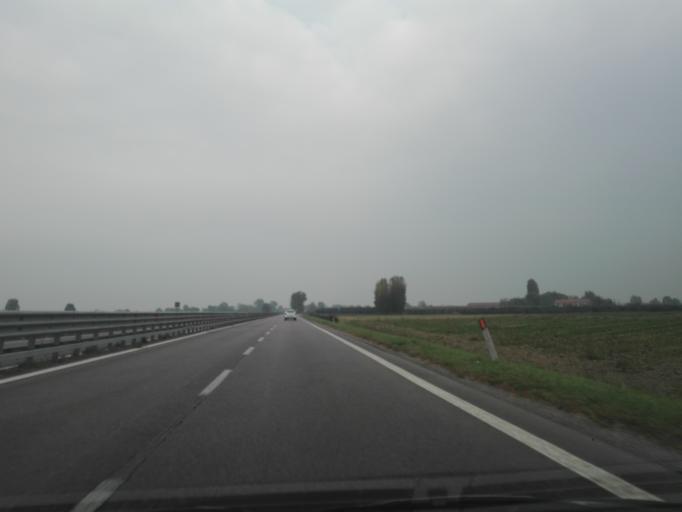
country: IT
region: Veneto
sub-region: Provincia di Verona
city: Villa Bartolomea
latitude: 45.1557
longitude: 11.3229
